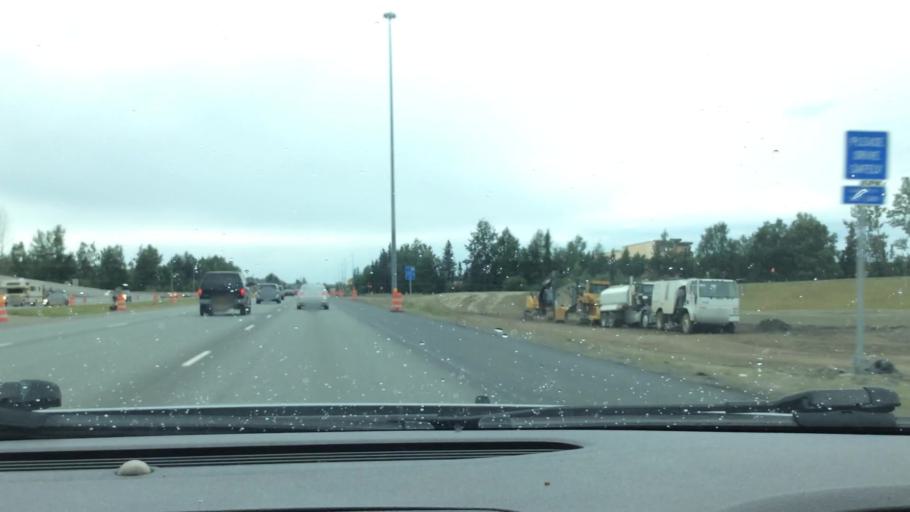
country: US
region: Alaska
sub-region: Anchorage Municipality
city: Elmendorf Air Force Base
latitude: 61.2270
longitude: -149.7348
